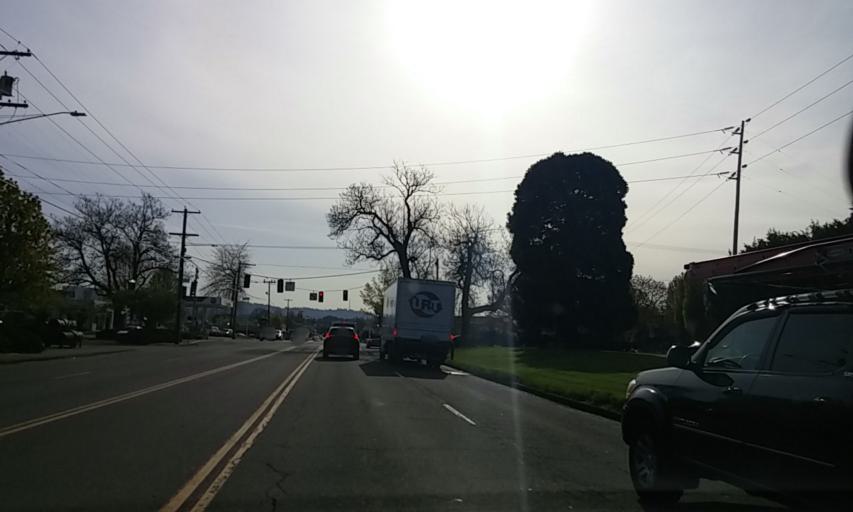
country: US
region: Oregon
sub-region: Washington County
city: Beaverton
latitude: 45.4882
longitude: -122.8119
